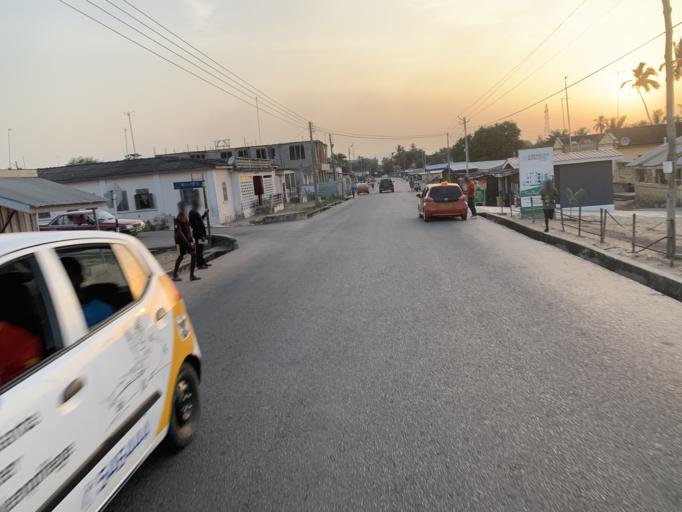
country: GH
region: Central
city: Winneba
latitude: 5.3508
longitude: -0.6225
